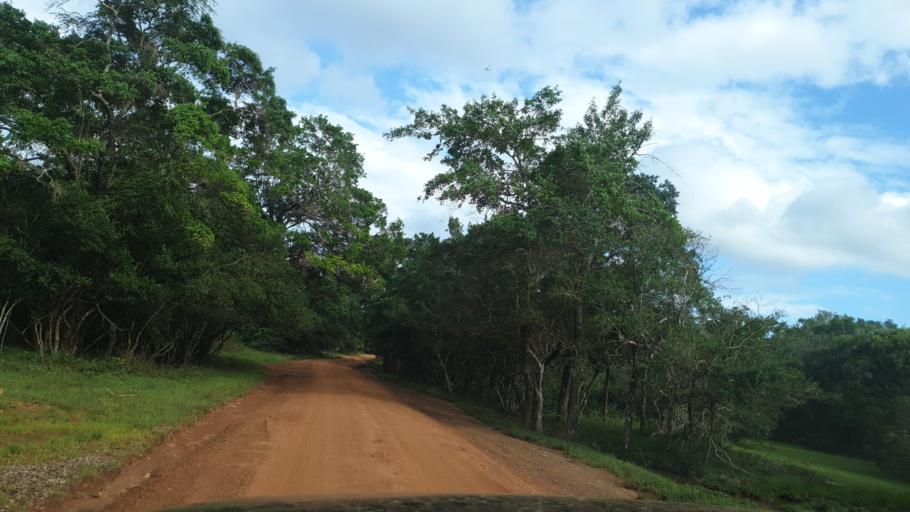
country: LK
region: North Central
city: Anuradhapura
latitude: 8.3636
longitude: 80.0984
